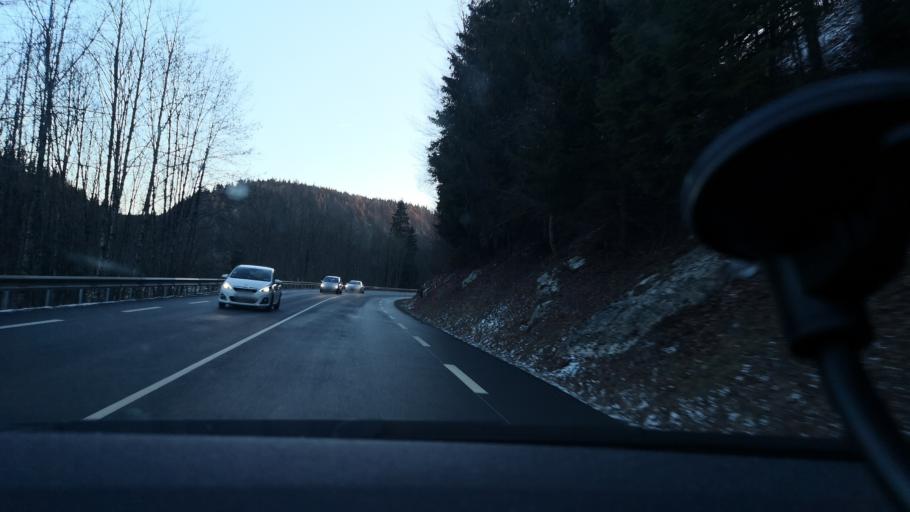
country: FR
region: Franche-Comte
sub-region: Departement du Doubs
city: La Cluse-et-Mijoux
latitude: 46.8707
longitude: 6.3644
